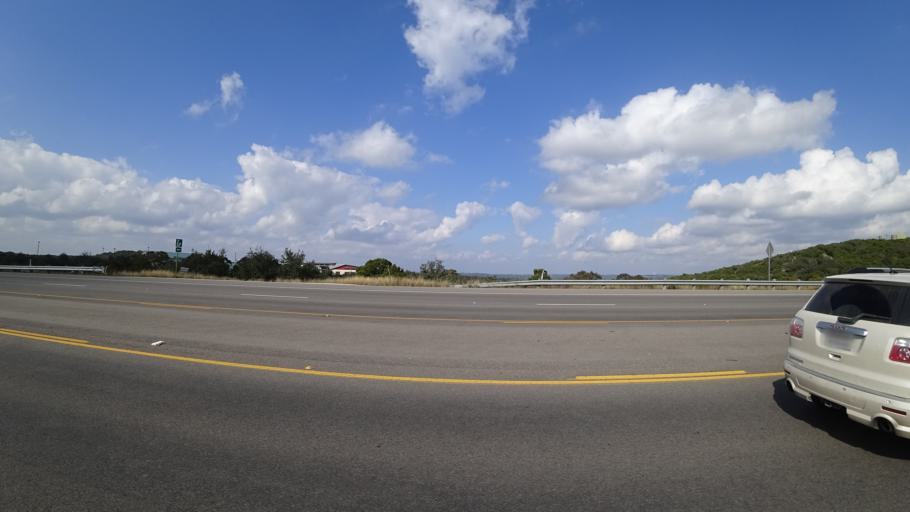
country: US
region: Texas
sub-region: Travis County
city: Barton Creek
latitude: 30.3174
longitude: -97.8693
